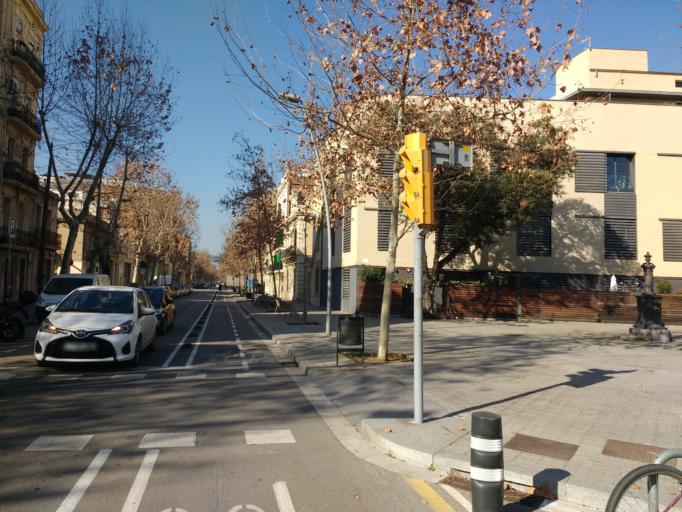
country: ES
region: Catalonia
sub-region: Provincia de Barcelona
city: Sant Marti
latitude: 41.3964
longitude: 2.2005
